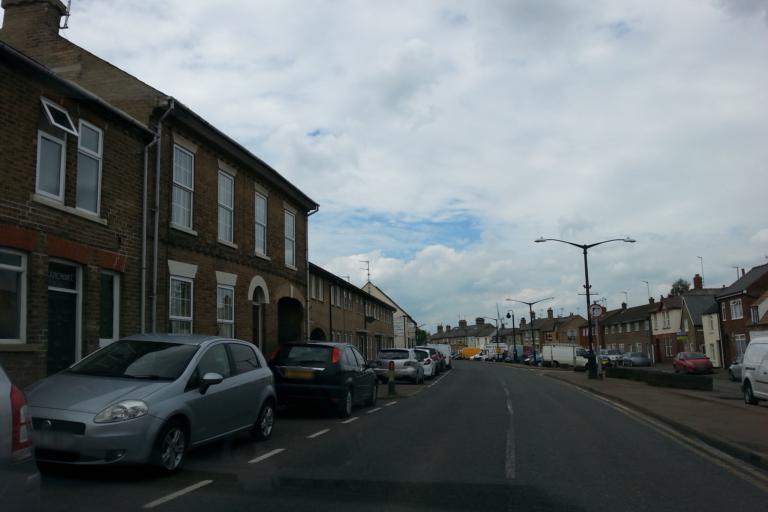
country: GB
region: England
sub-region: Cambridgeshire
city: Ramsey
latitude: 52.4506
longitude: -0.1081
